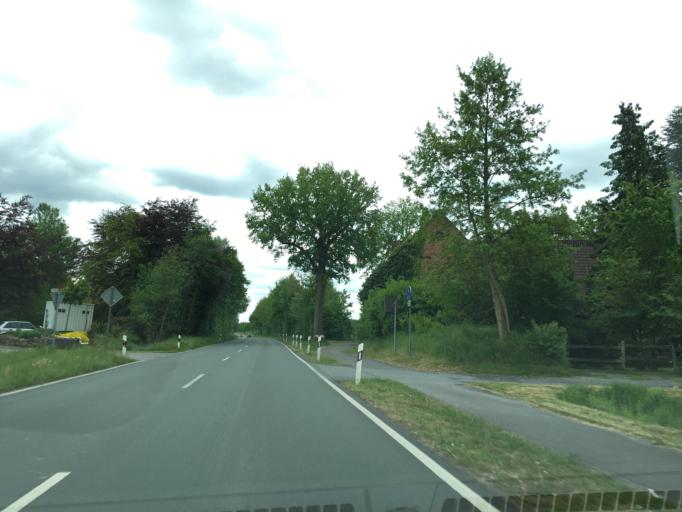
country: DE
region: North Rhine-Westphalia
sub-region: Regierungsbezirk Munster
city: Havixbeck
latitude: 51.9329
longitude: 7.4517
